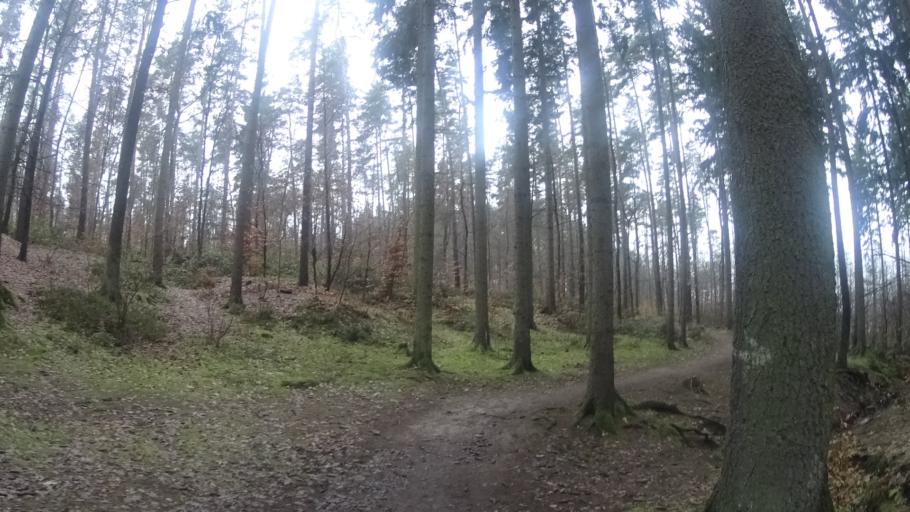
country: DE
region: Thuringia
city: Stadtroda
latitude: 50.8631
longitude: 11.7401
